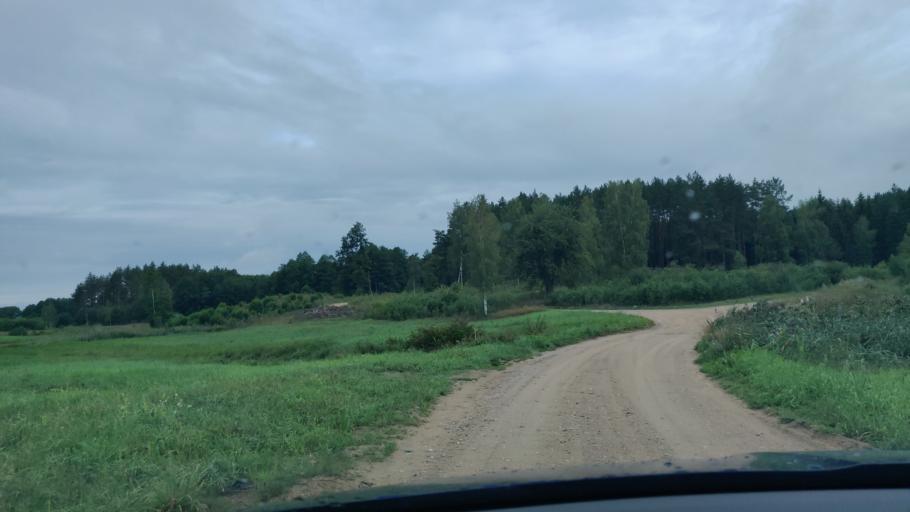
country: LT
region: Vilnius County
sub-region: Trakai
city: Rudiskes
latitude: 54.6049
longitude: 24.8465
